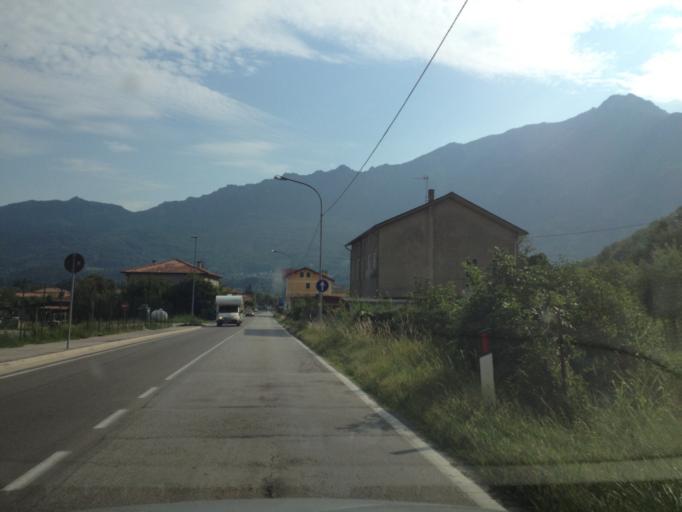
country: IT
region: Veneto
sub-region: Provincia di Vicenza
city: Arsiero
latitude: 45.8108
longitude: 11.3616
